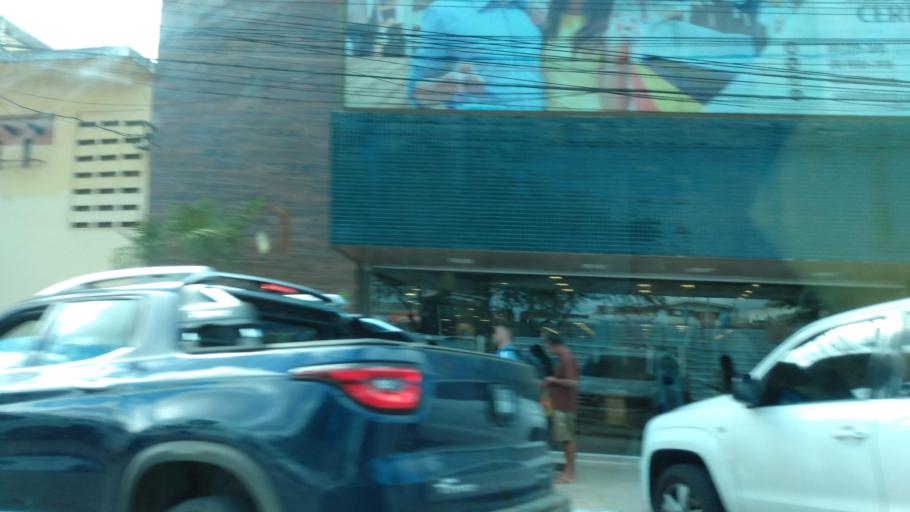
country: BR
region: Pernambuco
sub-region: Caruaru
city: Caruaru
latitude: -8.2927
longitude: -35.9854
